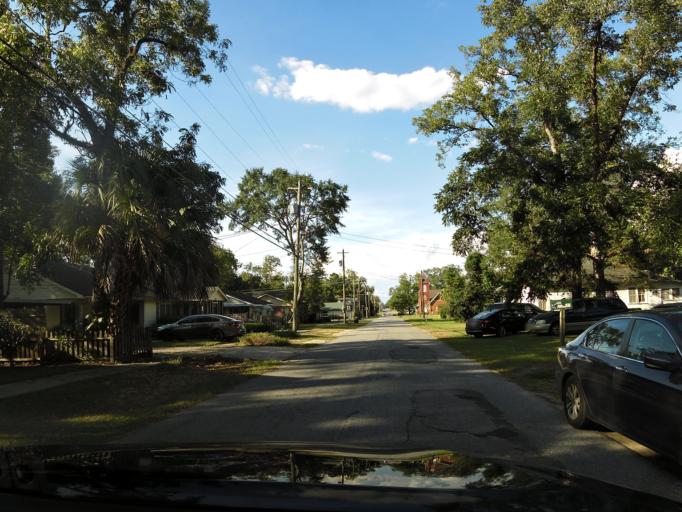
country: US
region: Georgia
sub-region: Brooks County
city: Quitman
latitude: 30.7758
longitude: -83.5577
